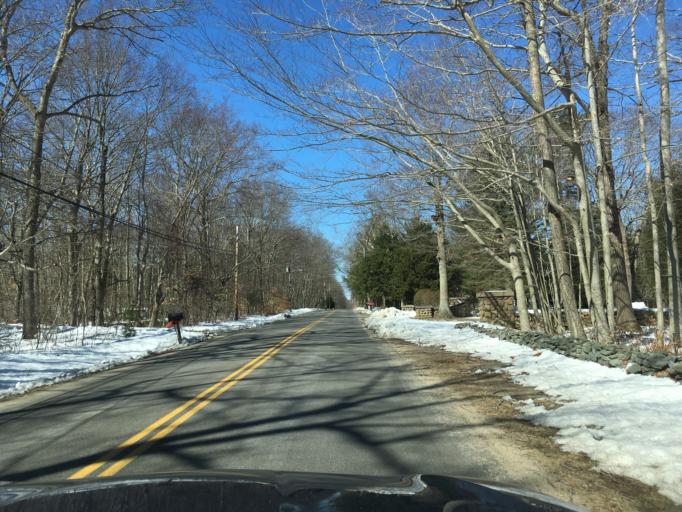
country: US
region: Rhode Island
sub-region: Washington County
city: Exeter
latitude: 41.6098
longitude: -71.5352
